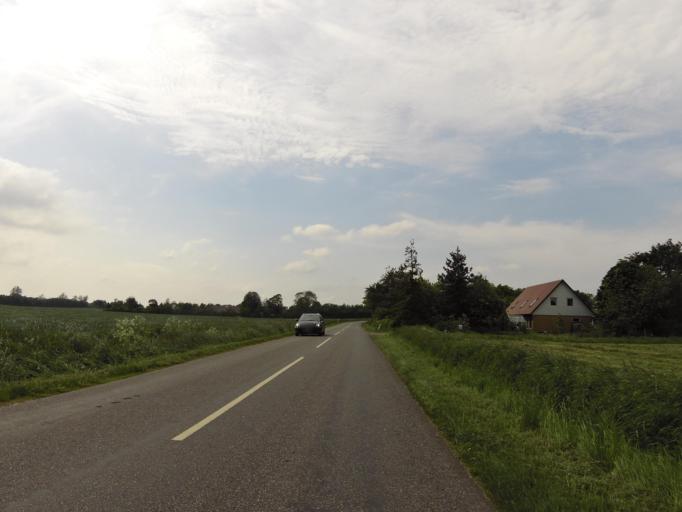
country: DK
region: South Denmark
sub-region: Haderslev Kommune
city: Gram
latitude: 55.2747
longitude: 9.1216
